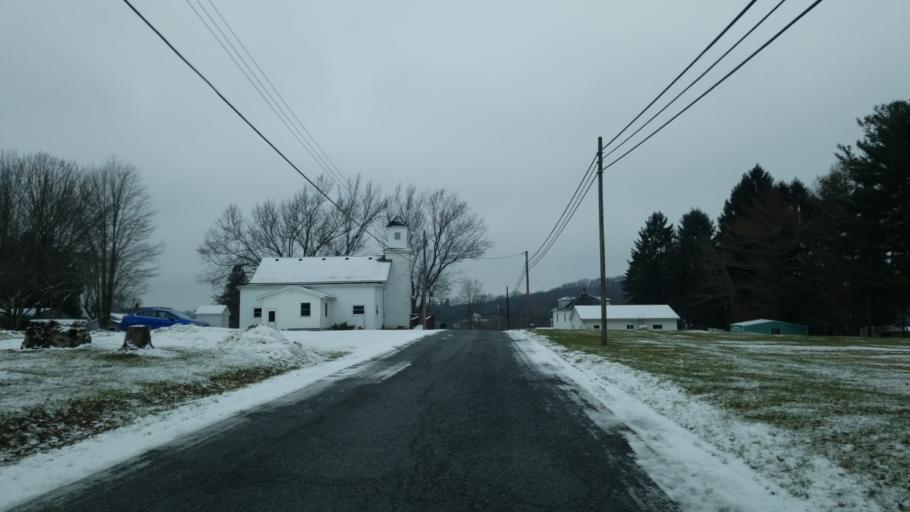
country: US
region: Pennsylvania
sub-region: Clearfield County
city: Sandy
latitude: 41.0777
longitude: -78.7870
